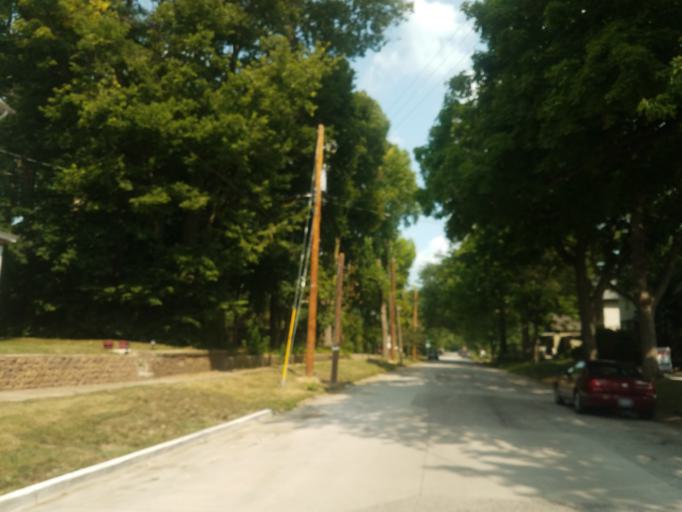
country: US
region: Illinois
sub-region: McLean County
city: Bloomington
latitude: 40.4770
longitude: -88.9898
